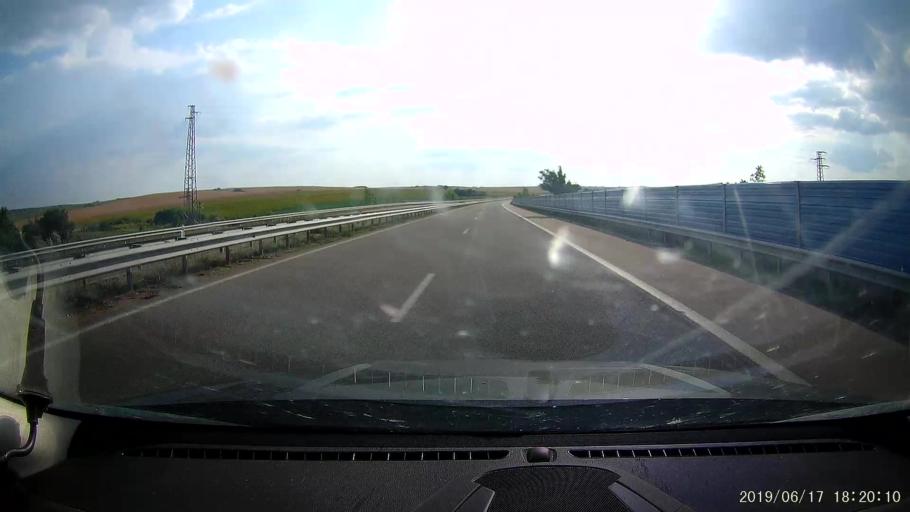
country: BG
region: Khaskovo
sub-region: Obshtina Simeonovgrad
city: Simeonovgrad
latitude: 41.9621
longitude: 25.8229
